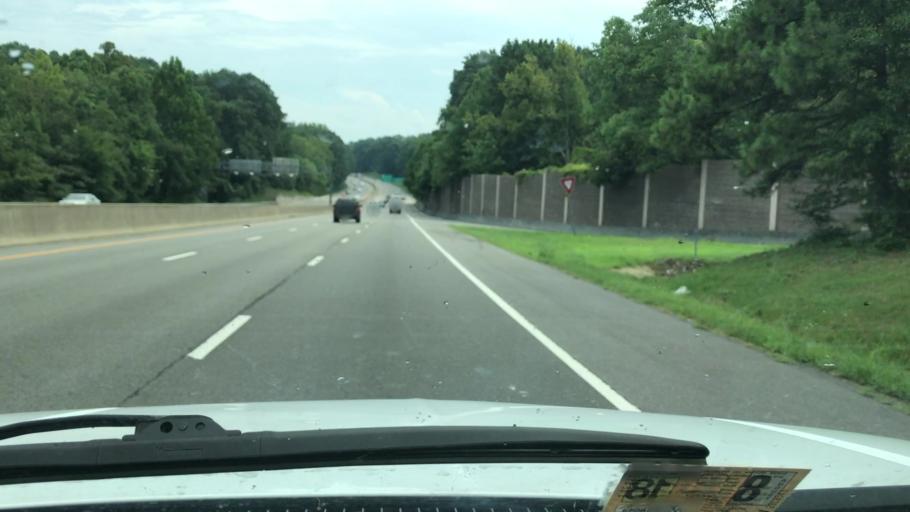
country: US
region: Virginia
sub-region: Chesterfield County
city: Bensley
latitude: 37.4603
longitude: -77.4971
